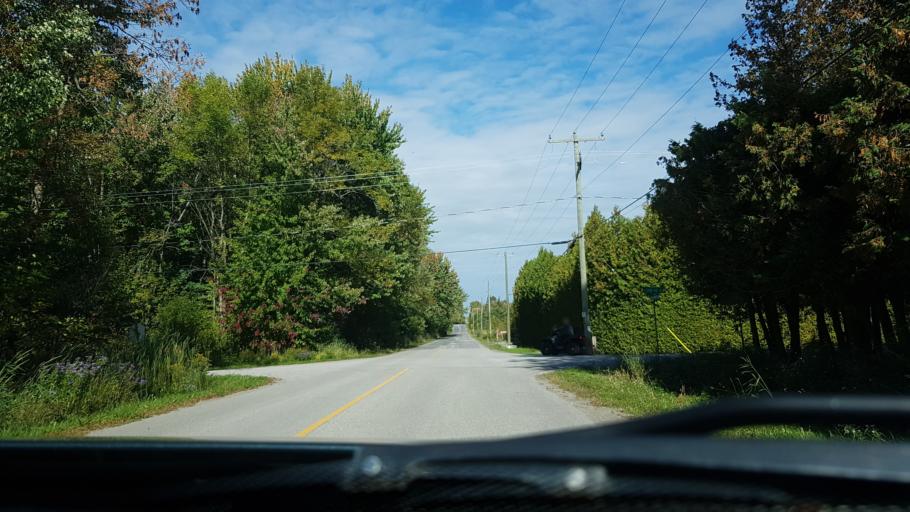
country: CA
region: Ontario
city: Orillia
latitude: 44.5930
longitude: -79.3175
